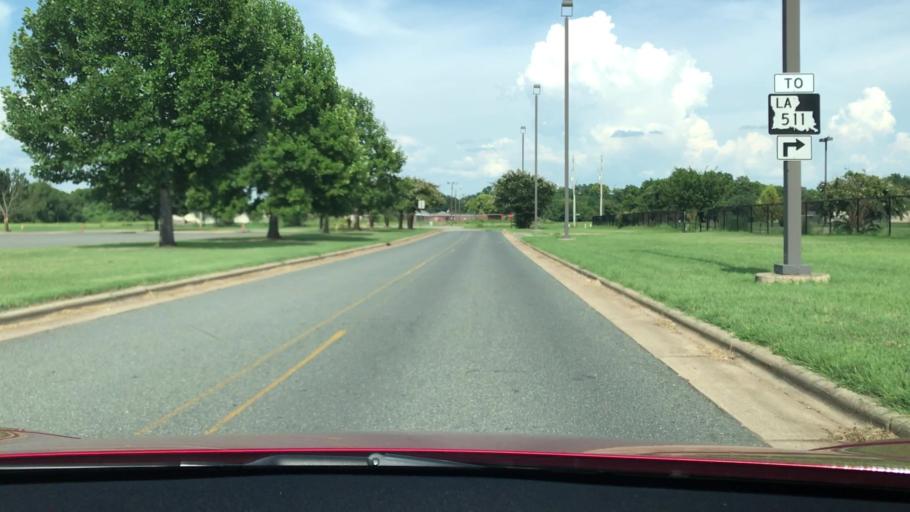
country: US
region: Louisiana
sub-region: Bossier Parish
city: Bossier City
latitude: 32.4623
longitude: -93.6735
